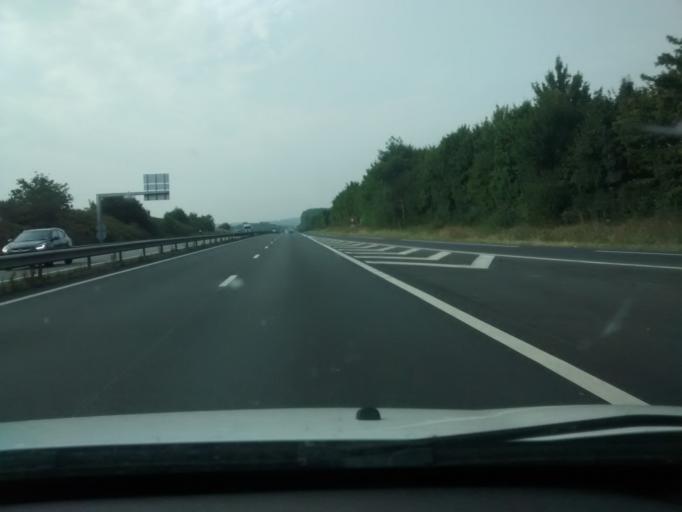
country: FR
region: Brittany
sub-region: Departement d'Ille-et-Vilaine
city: Chartres-de-Bretagne
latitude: 48.0176
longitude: -1.6913
